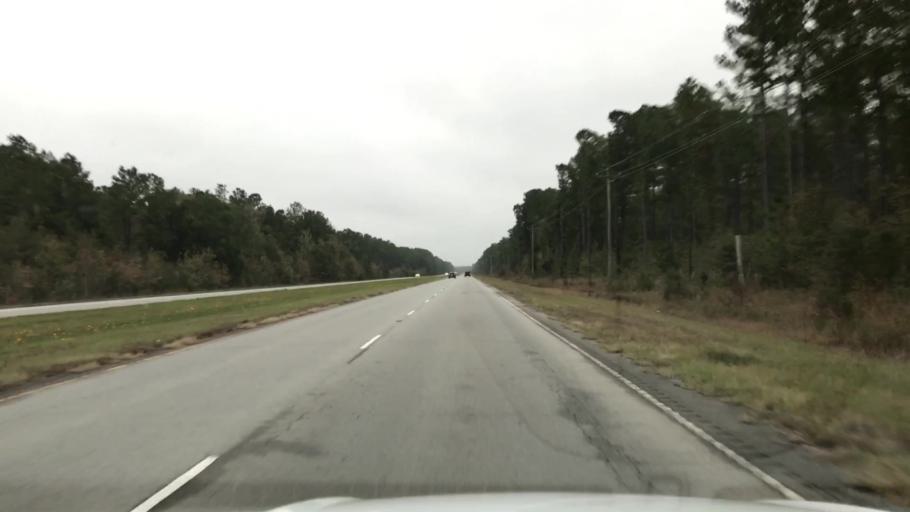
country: US
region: South Carolina
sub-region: Charleston County
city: Awendaw
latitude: 33.0077
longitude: -79.6401
